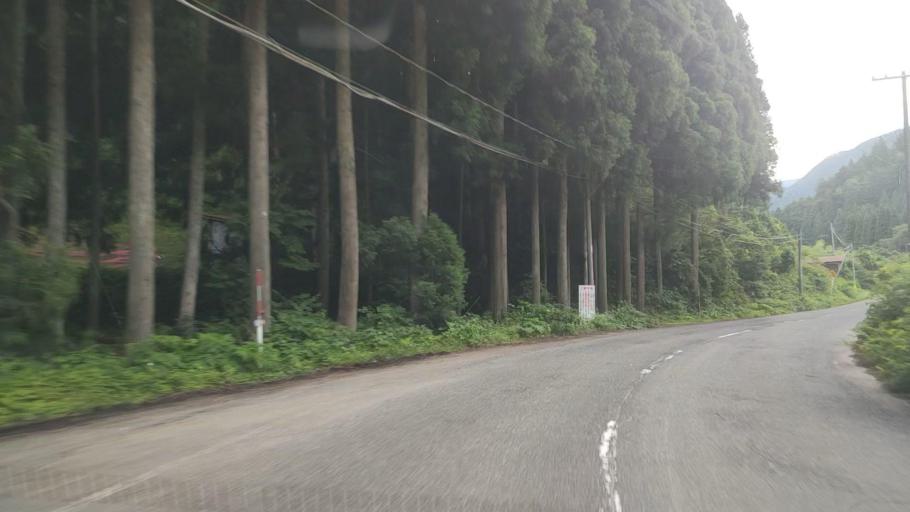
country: JP
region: Tottori
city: Tottori
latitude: 35.3302
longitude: 134.0609
